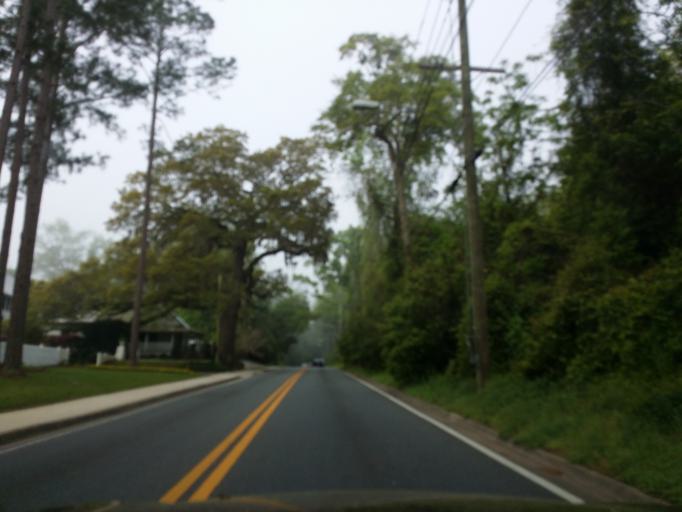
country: US
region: Florida
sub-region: Leon County
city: Tallahassee
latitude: 30.4661
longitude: -84.2542
